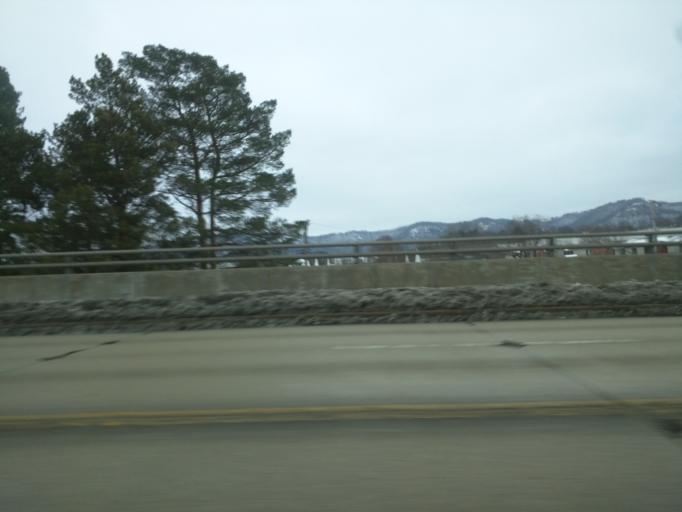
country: US
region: Wisconsin
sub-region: La Crosse County
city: North La Crosse
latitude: 43.8373
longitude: -91.2396
